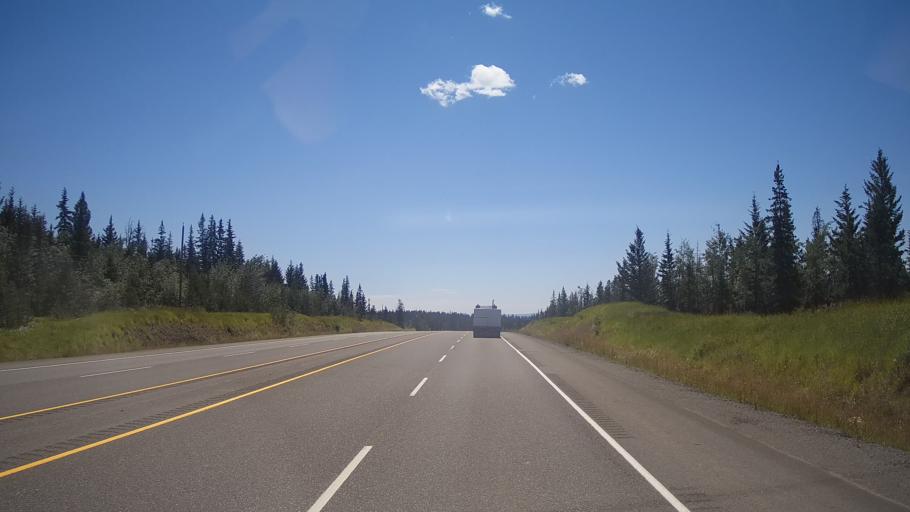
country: CA
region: British Columbia
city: Cache Creek
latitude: 51.3925
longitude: -121.3700
